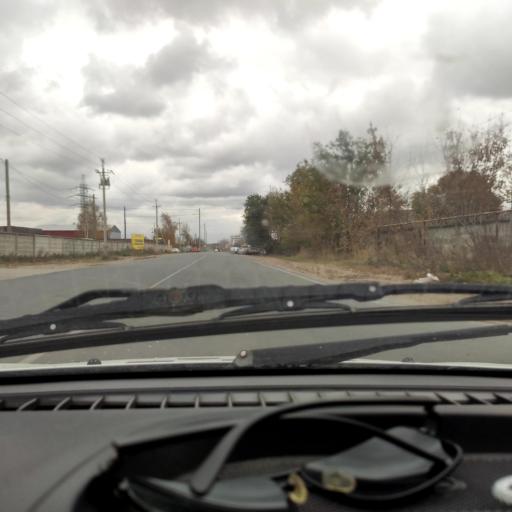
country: RU
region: Samara
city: Tol'yatti
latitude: 53.5286
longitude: 49.4733
